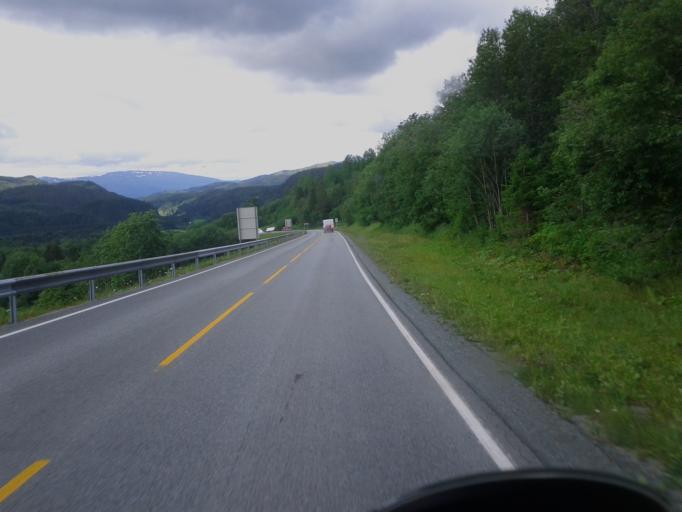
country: NO
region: Nord-Trondelag
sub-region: Grong
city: Grong
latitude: 64.5354
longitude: 12.4153
